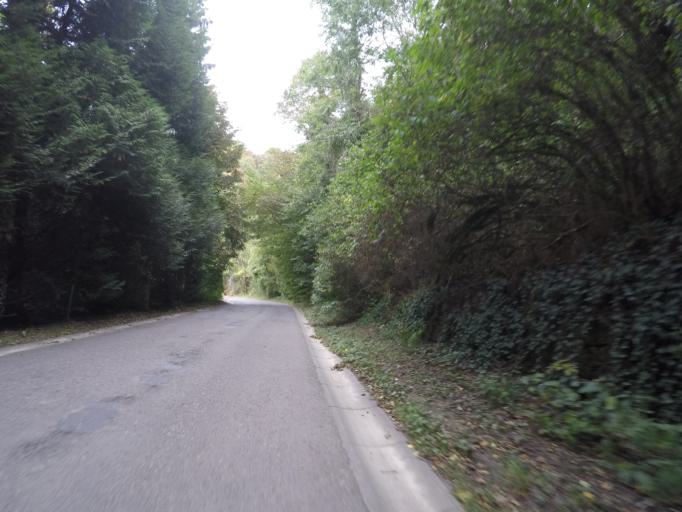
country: BE
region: Wallonia
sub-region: Province de Namur
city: Dinant
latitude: 50.2749
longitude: 4.9462
